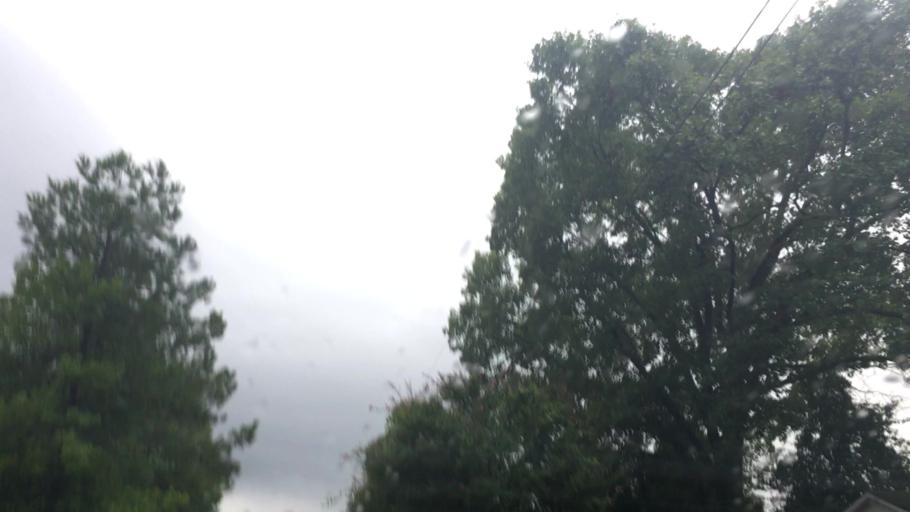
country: US
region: Alabama
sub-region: Tuscaloosa County
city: Northport
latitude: 33.2432
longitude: -87.5846
